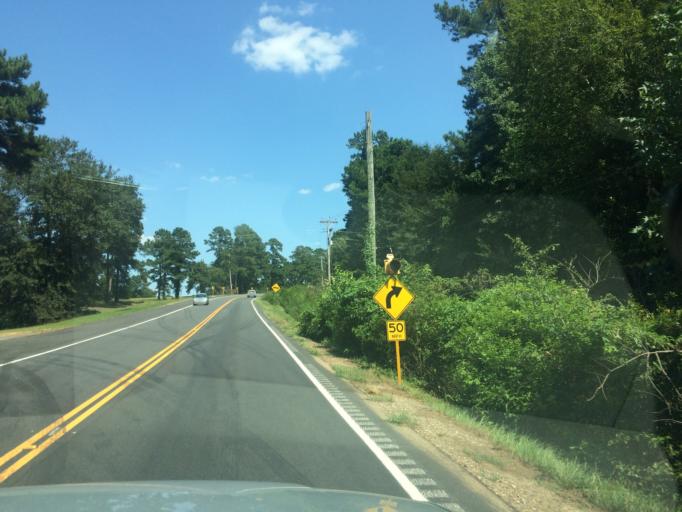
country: US
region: South Carolina
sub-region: Barnwell County
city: Williston
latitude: 33.5818
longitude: -81.5100
